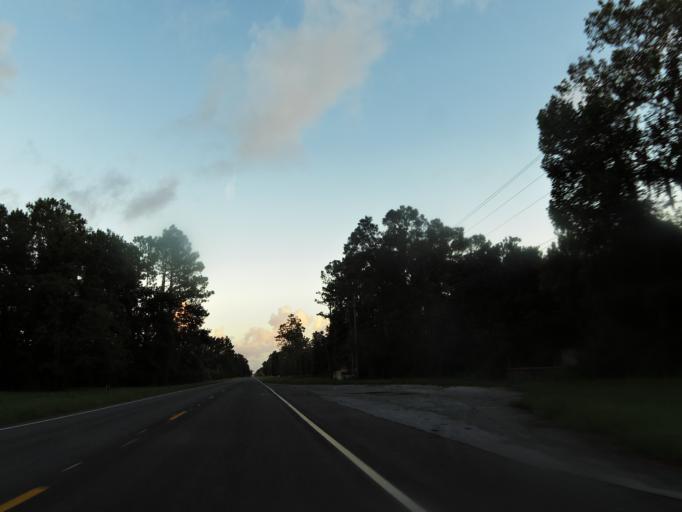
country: US
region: Georgia
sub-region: Camden County
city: Kingsland
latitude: 30.8754
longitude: -81.7056
